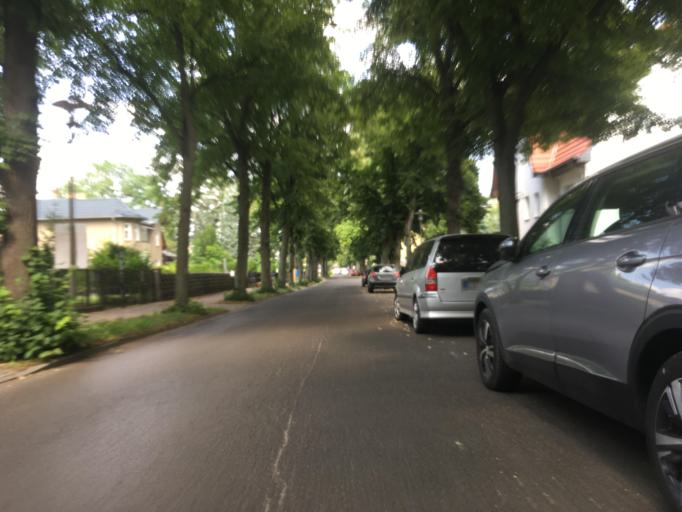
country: DE
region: Brandenburg
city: Zeuthen
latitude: 52.3468
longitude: 13.6229
